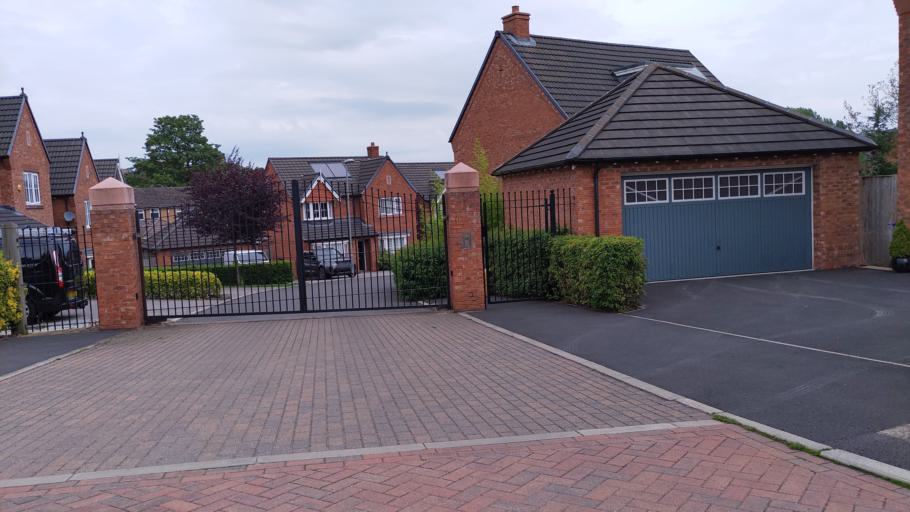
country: GB
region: England
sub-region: Lancashire
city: Chorley
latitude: 53.6387
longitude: -2.6257
